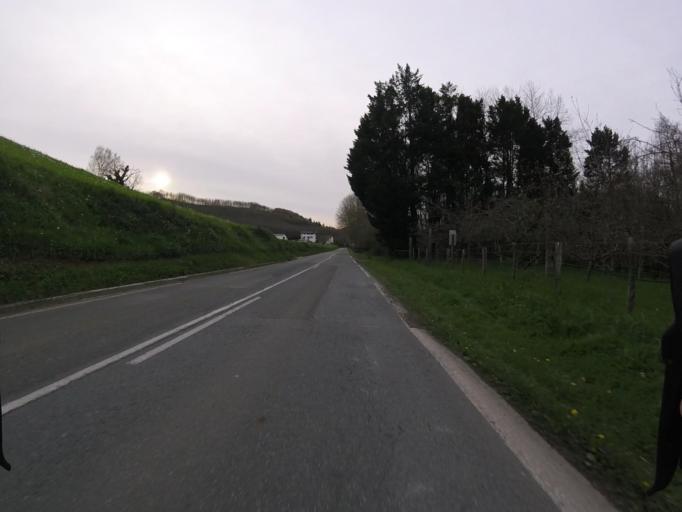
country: ES
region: Basque Country
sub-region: Provincia de Guipuzcoa
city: Errenteria
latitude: 43.2942
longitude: -1.8682
